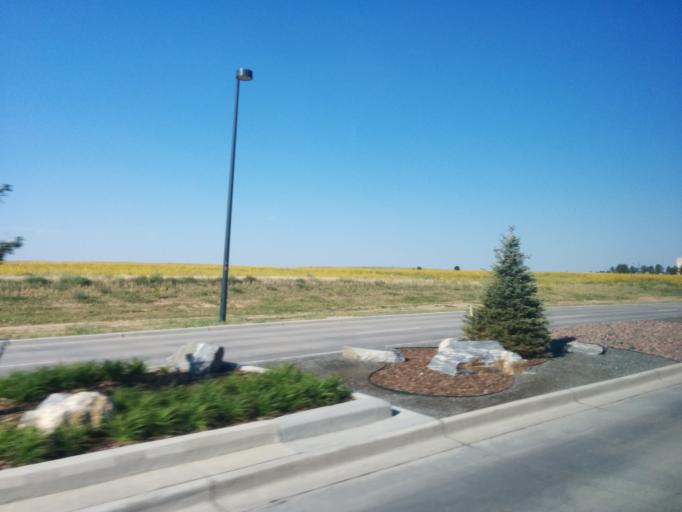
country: US
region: Colorado
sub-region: Adams County
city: Aurora
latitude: 39.7727
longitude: -104.7856
